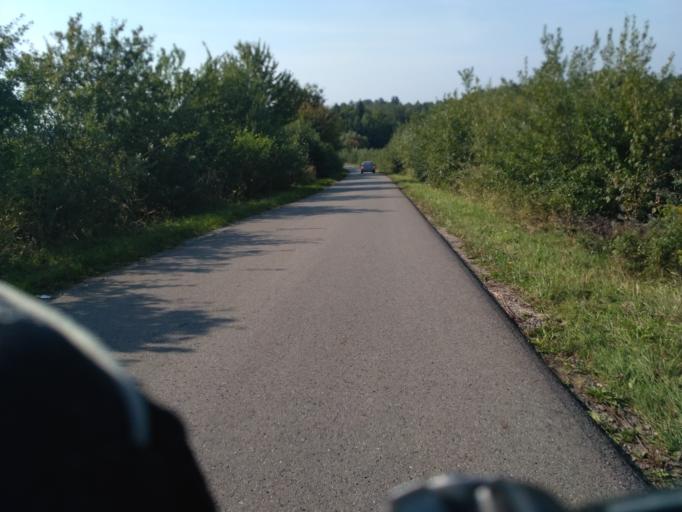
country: PL
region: Subcarpathian Voivodeship
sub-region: Powiat brzozowski
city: Golcowa
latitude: 49.7970
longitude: 22.0253
